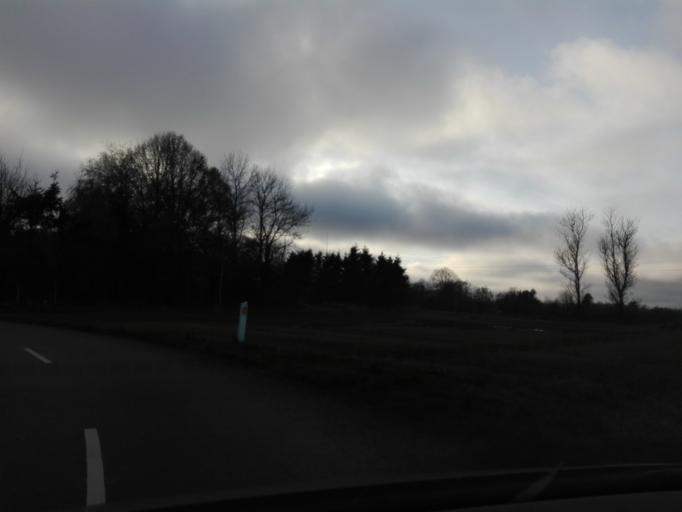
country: DK
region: Central Jutland
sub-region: Arhus Kommune
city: Solbjerg
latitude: 56.0355
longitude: 10.1037
